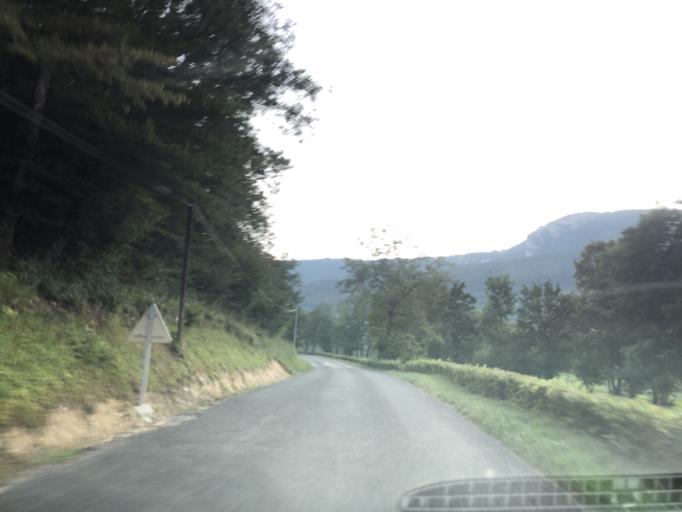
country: FR
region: Rhone-Alpes
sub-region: Departement de l'Ain
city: Belley
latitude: 45.7799
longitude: 5.6235
